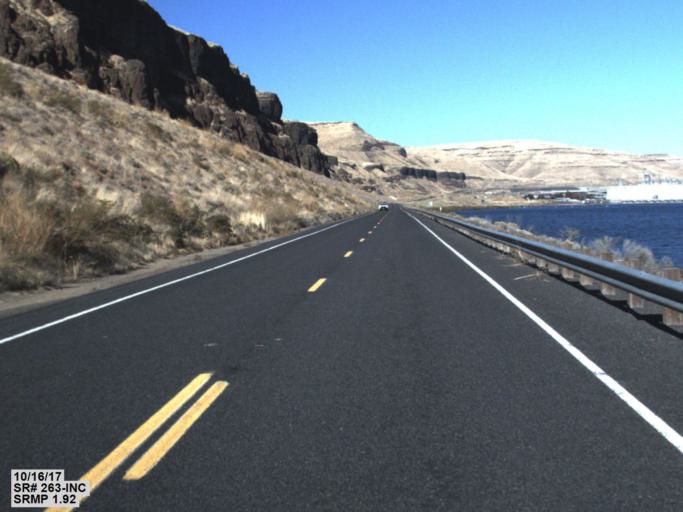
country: US
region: Washington
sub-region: Franklin County
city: Connell
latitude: 46.5482
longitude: -118.5559
